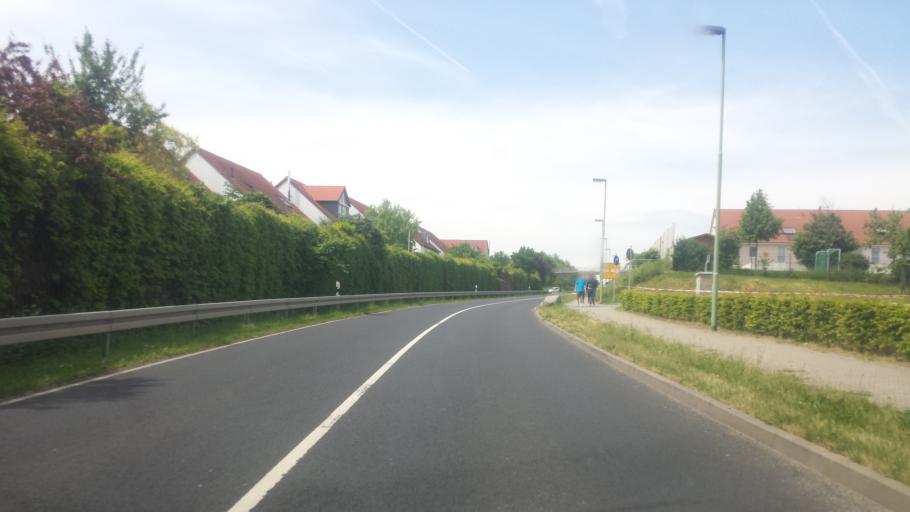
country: DE
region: Hesse
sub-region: Regierungsbezirk Darmstadt
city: Bad Vilbel
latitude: 50.2110
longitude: 8.7439
